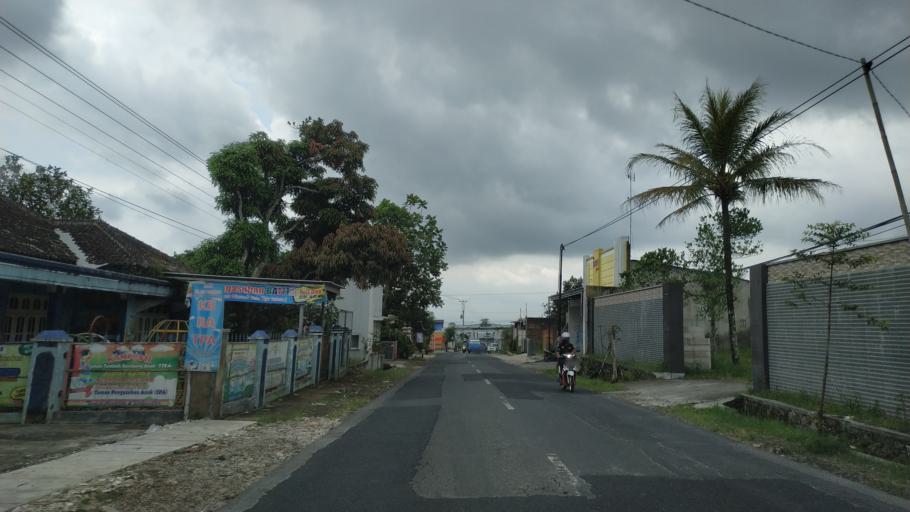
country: ID
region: Central Java
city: Magelang
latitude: -7.2859
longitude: 110.1179
